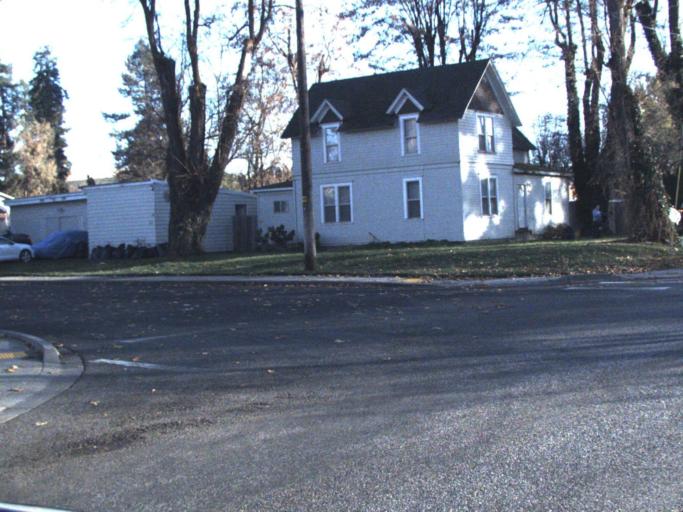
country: US
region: Washington
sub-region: Walla Walla County
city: Waitsburg
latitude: 46.2647
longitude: -118.1532
